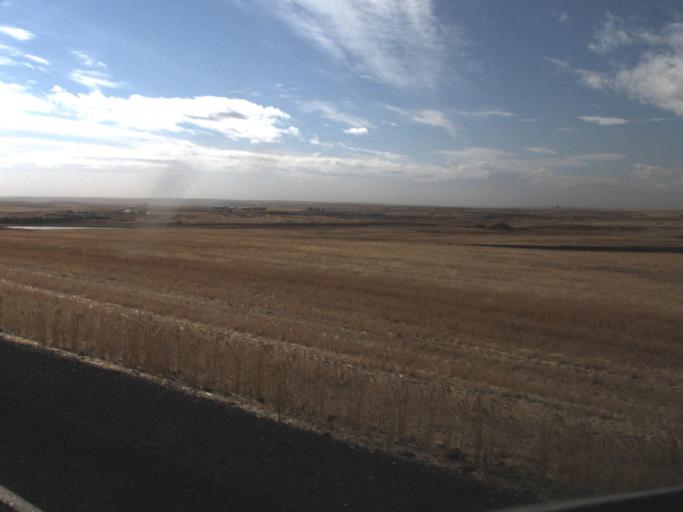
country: US
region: Washington
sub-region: Okanogan County
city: Coulee Dam
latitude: 47.7790
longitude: -118.7220
